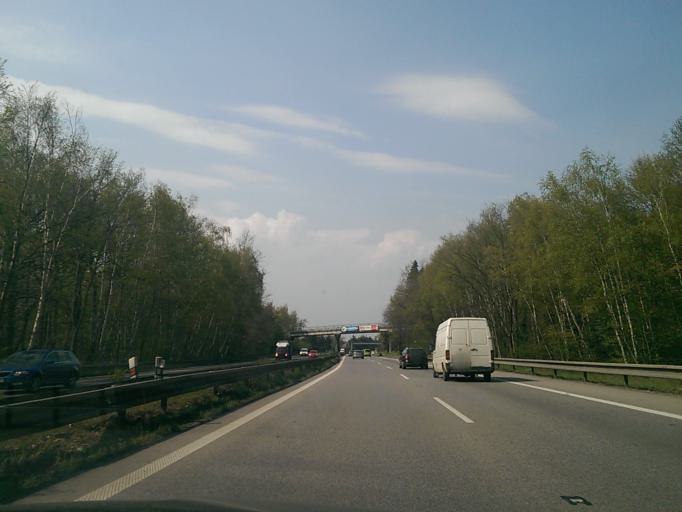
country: CZ
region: Central Bohemia
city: Brandys nad Labem-Stara Boleslav
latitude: 50.1925
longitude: 14.6947
